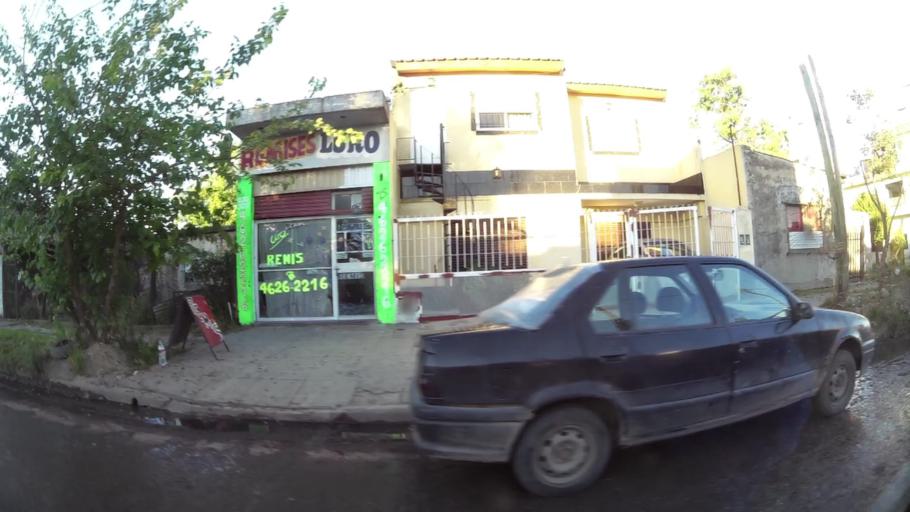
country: AR
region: Buenos Aires
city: San Justo
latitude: -34.7317
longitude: -58.6093
